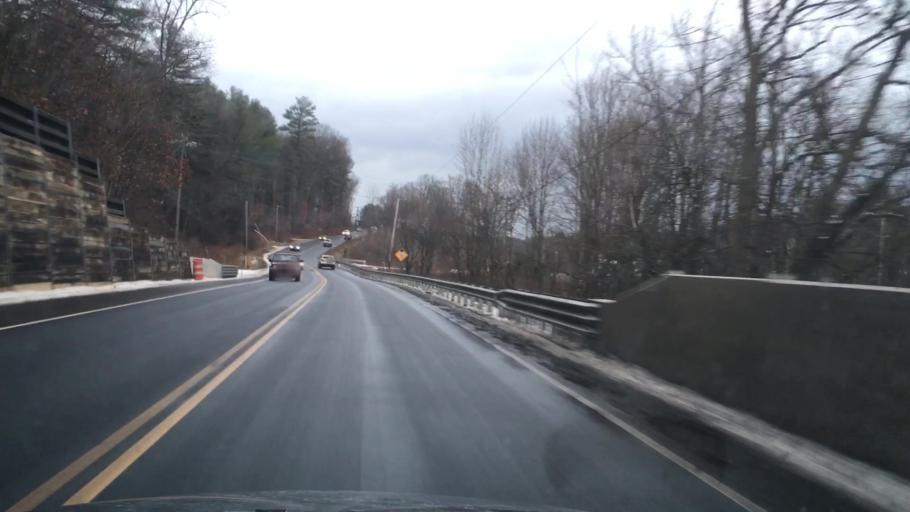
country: US
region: New Hampshire
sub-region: Sullivan County
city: Claremont
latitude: 43.3939
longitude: -72.3871
